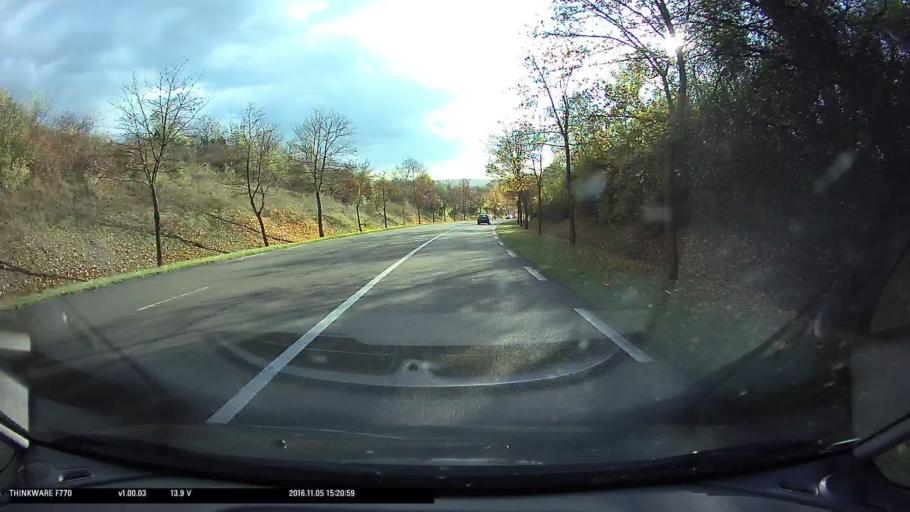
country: FR
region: Ile-de-France
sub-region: Departement du Val-d'Oise
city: Sagy
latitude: 49.0572
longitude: 1.9626
